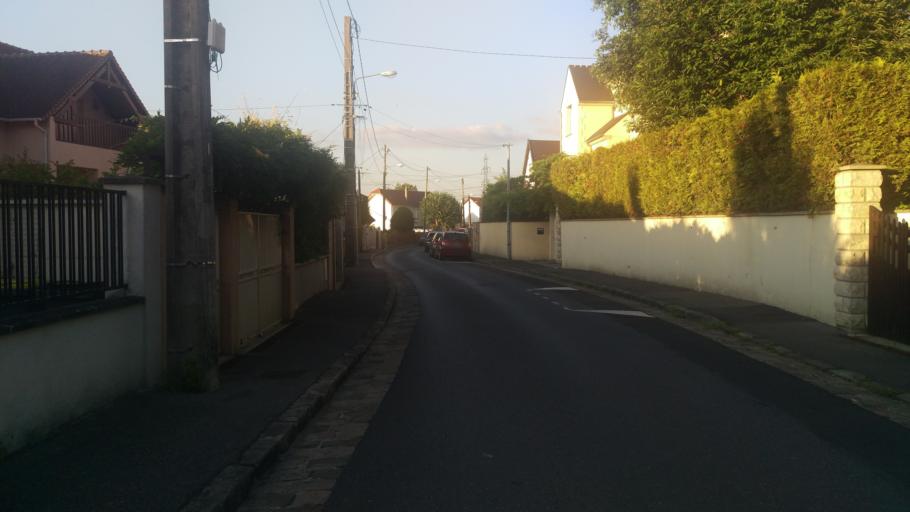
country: FR
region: Ile-de-France
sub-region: Departement de l'Essonne
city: Igny
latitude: 48.7271
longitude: 2.2332
